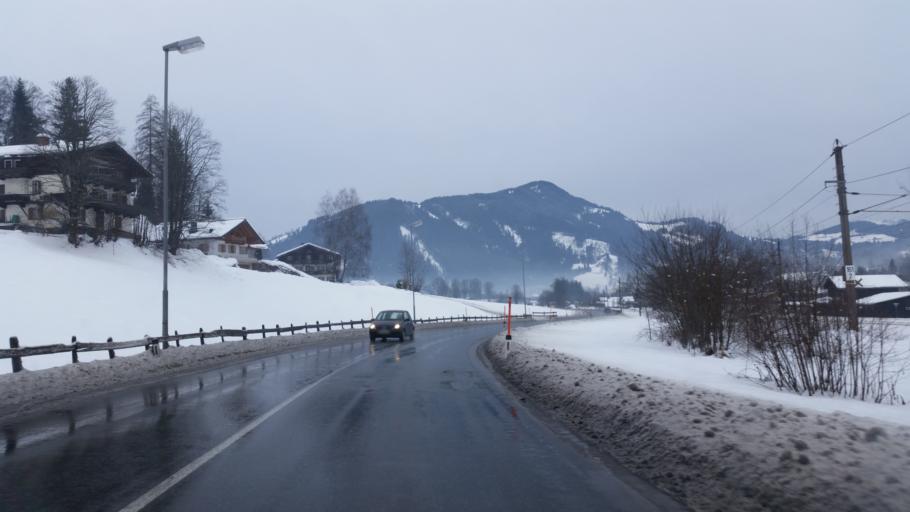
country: AT
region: Tyrol
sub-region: Politischer Bezirk Kitzbuhel
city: Reith bei Kitzbuhel
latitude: 47.4543
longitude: 12.3680
